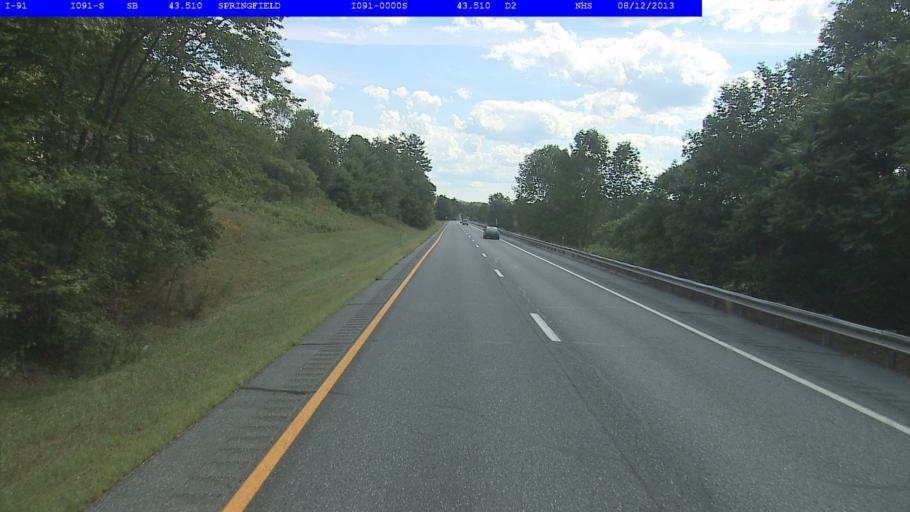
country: US
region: New Hampshire
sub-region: Sullivan County
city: Charlestown
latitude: 43.2917
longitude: -72.4276
